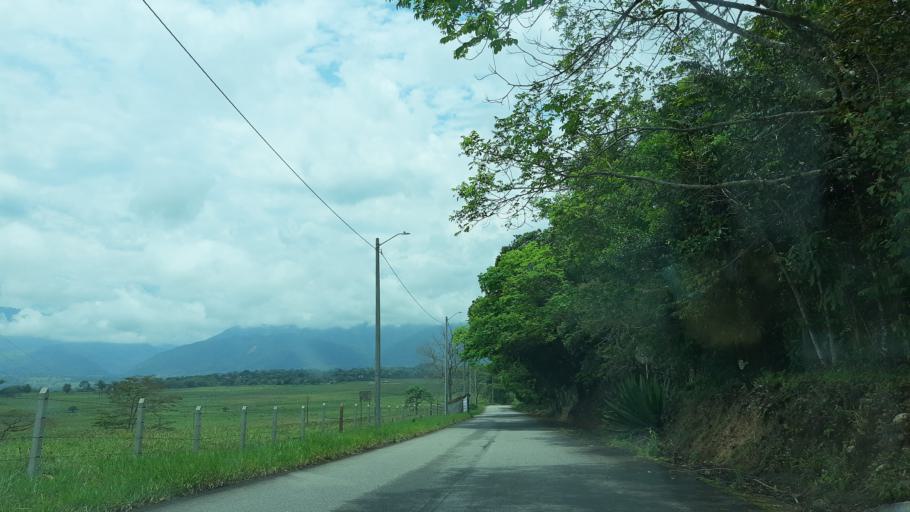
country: CO
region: Casanare
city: Sabanalarga
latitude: 4.8371
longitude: -73.0428
